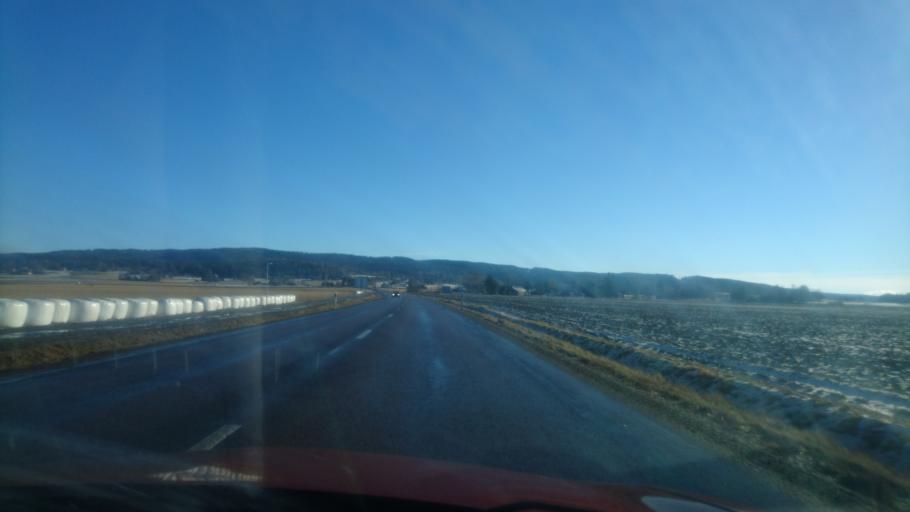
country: SE
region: Vaermland
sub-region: Sunne Kommun
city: Sunne
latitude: 59.8385
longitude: 13.1671
